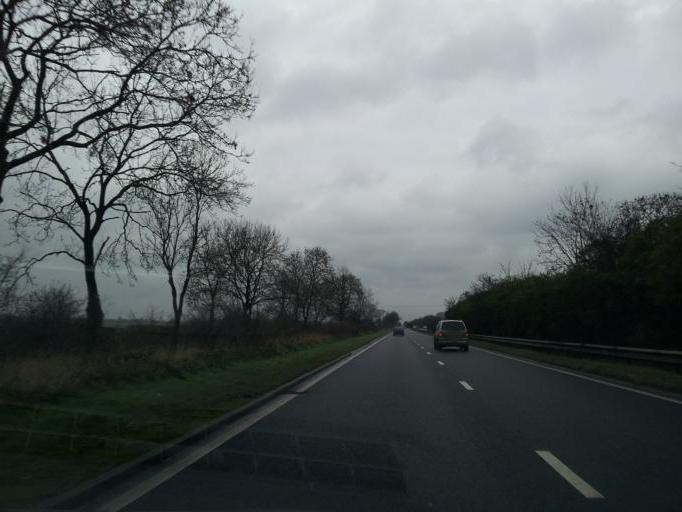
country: GB
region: England
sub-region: Leicestershire
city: Queniborough
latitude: 52.7554
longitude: -1.0590
